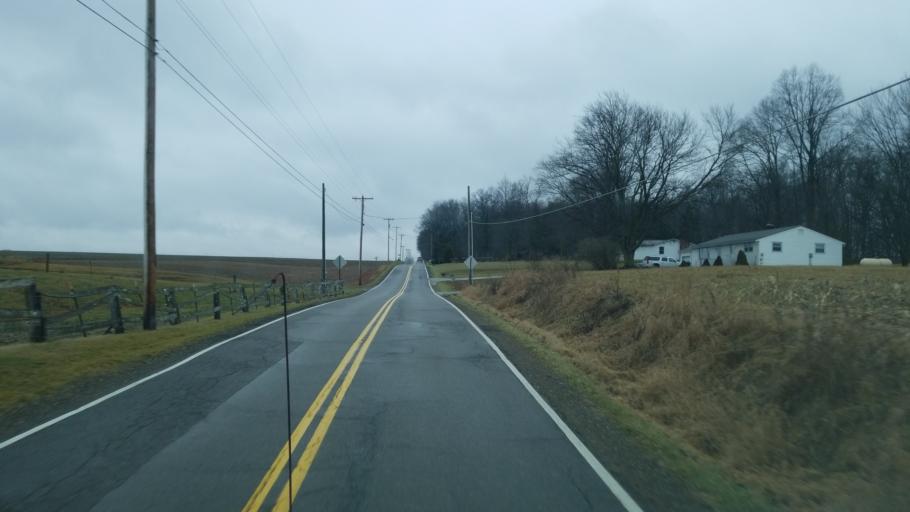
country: US
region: Ohio
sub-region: Wayne County
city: Rittman
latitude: 40.9153
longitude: -81.7824
